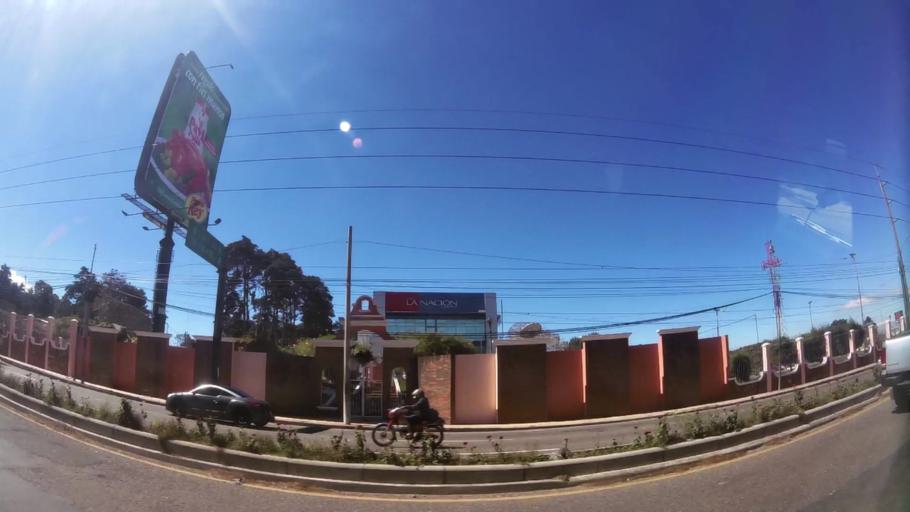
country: GT
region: Guatemala
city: San Jose Pinula
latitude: 14.5449
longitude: -90.4543
